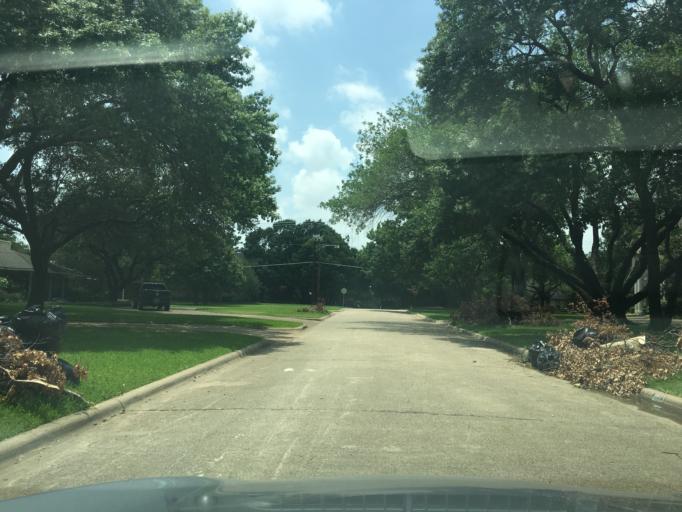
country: US
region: Texas
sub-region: Dallas County
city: University Park
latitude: 32.8986
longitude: -96.8286
